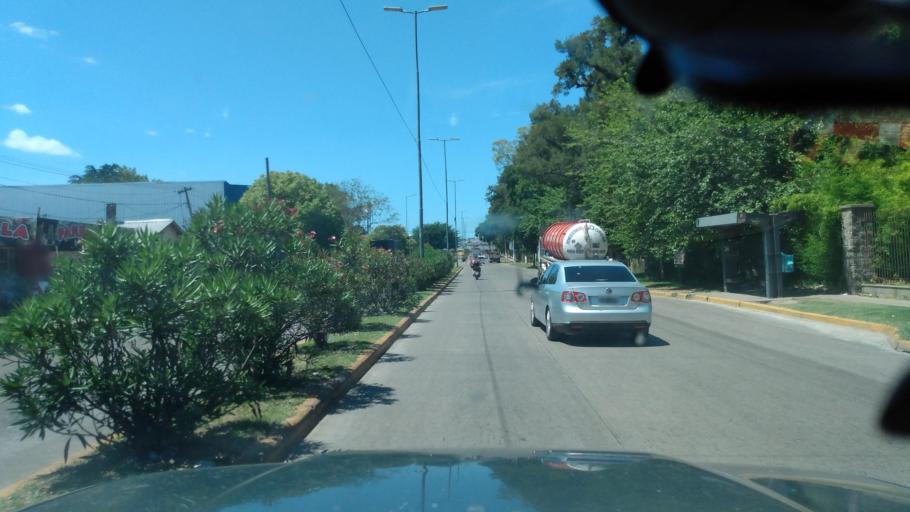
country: AR
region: Buenos Aires
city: Hurlingham
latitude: -34.5536
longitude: -58.7240
